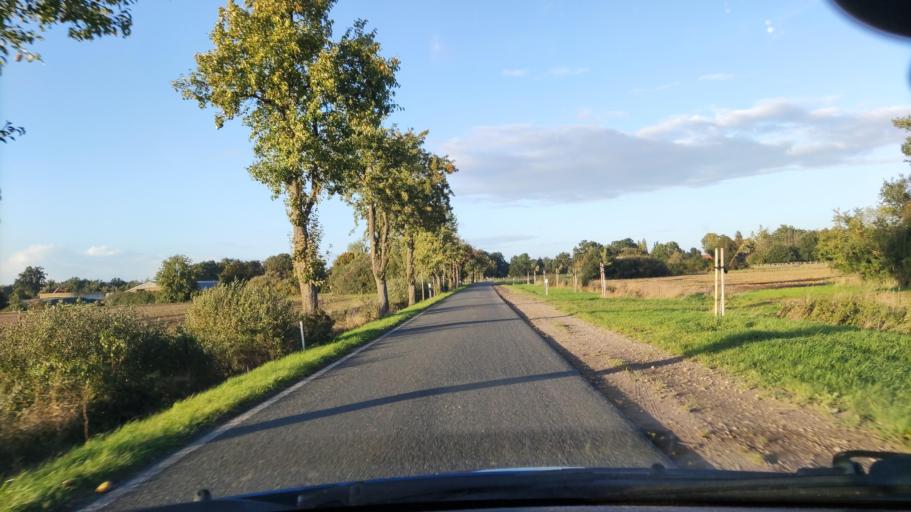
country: DE
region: Lower Saxony
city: Neu Darchau
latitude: 53.2831
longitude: 10.8740
